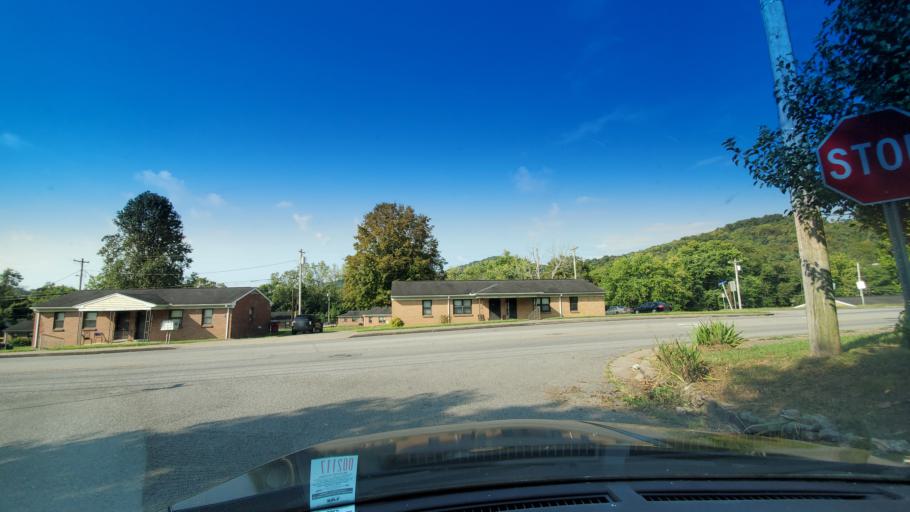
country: US
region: Tennessee
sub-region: Smith County
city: Carthage
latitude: 36.2474
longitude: -85.9494
